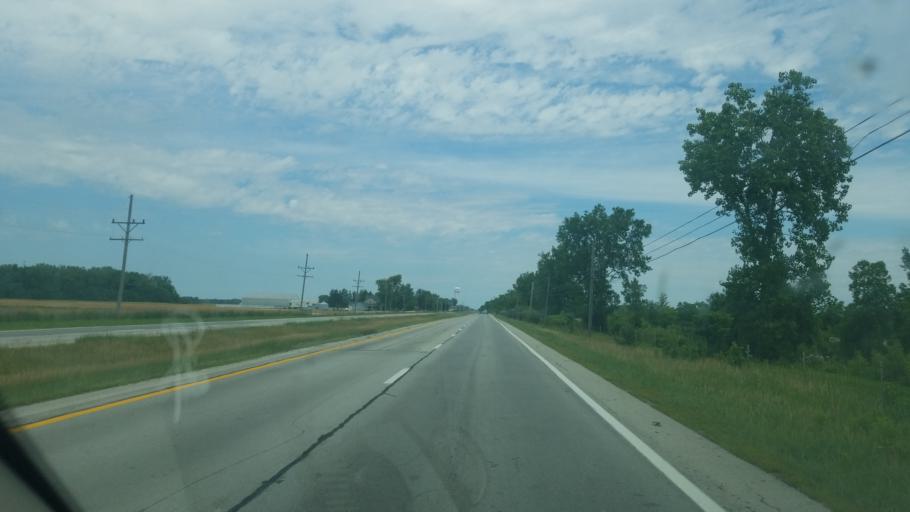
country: US
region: Ohio
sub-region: Wood County
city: North Baltimore
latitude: 41.2564
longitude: -83.6500
